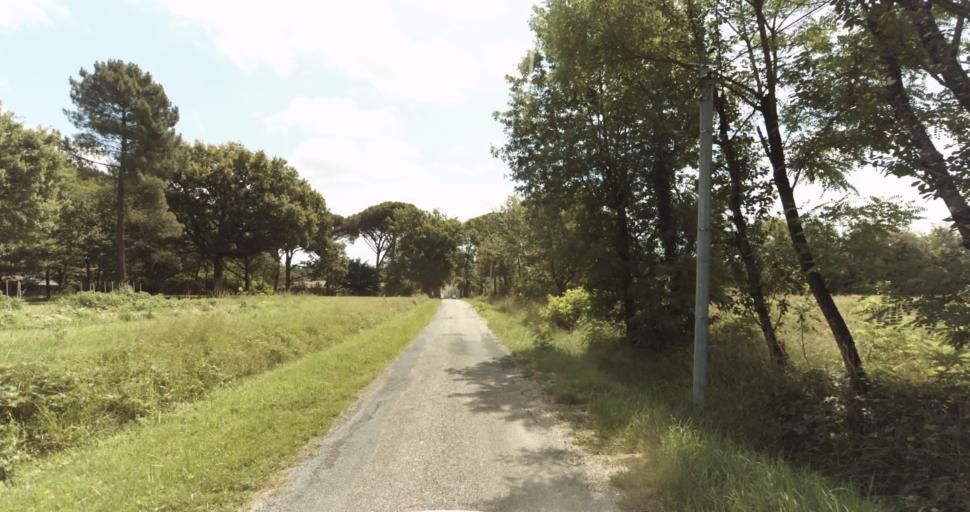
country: FR
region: Aquitaine
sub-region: Departement de la Gironde
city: Bazas
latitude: 44.4659
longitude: -0.1732
